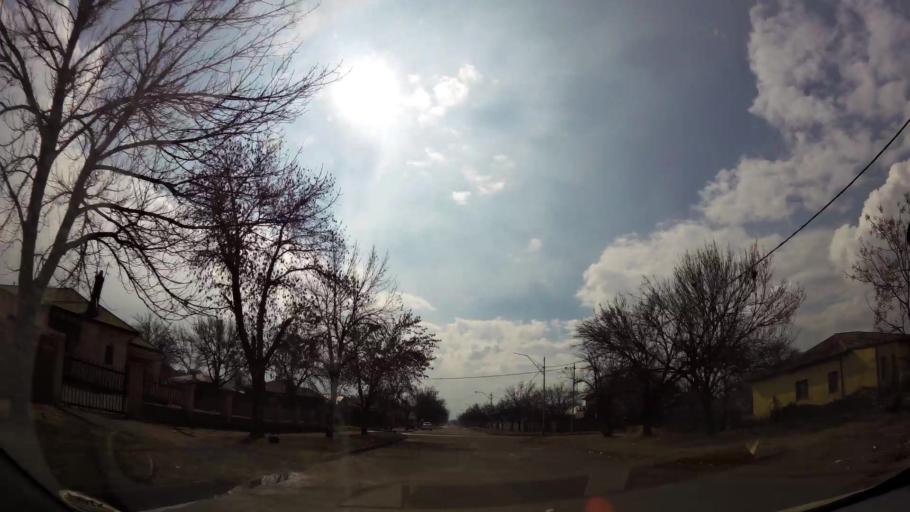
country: ZA
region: Gauteng
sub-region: Sedibeng District Municipality
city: Vereeniging
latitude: -26.6788
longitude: 27.9197
